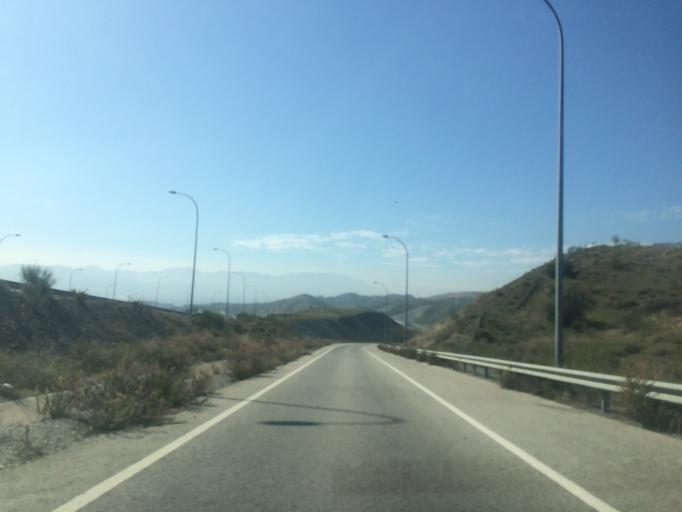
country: ES
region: Andalusia
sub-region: Provincia de Malaga
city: Malaga
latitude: 36.7561
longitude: -4.4861
